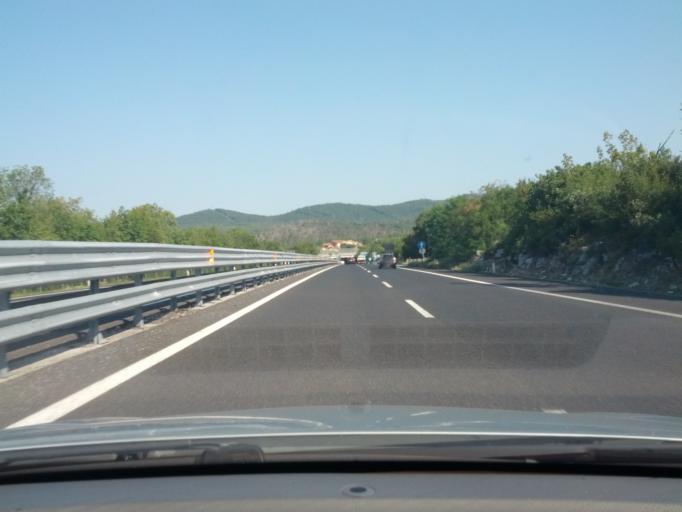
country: IT
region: Friuli Venezia Giulia
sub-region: Provincia di Trieste
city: Sistiana-Visogliano
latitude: 45.7700
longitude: 13.6452
